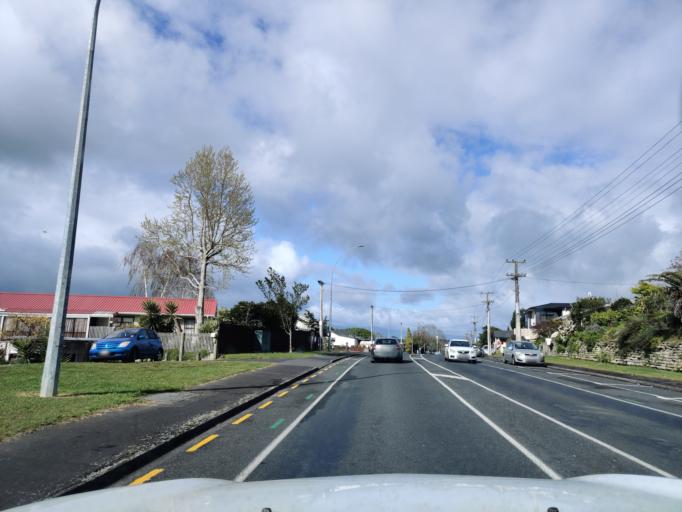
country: NZ
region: Waikato
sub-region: Hamilton City
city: Hamilton
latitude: -37.8020
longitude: 175.2454
